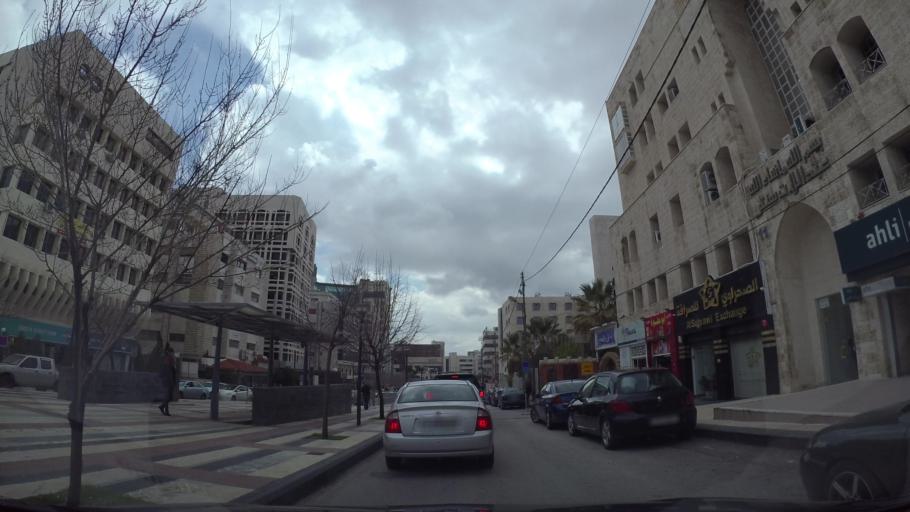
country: JO
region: Amman
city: Amman
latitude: 31.9689
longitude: 35.8990
